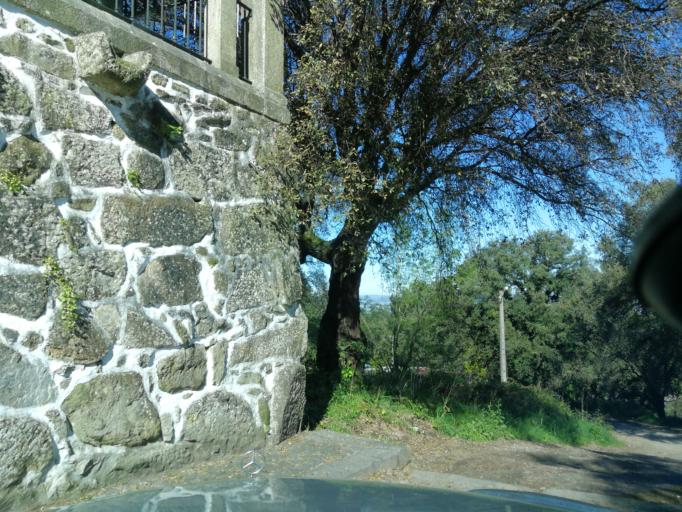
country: PT
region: Braga
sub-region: Braga
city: Braga
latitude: 41.5427
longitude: -8.4453
